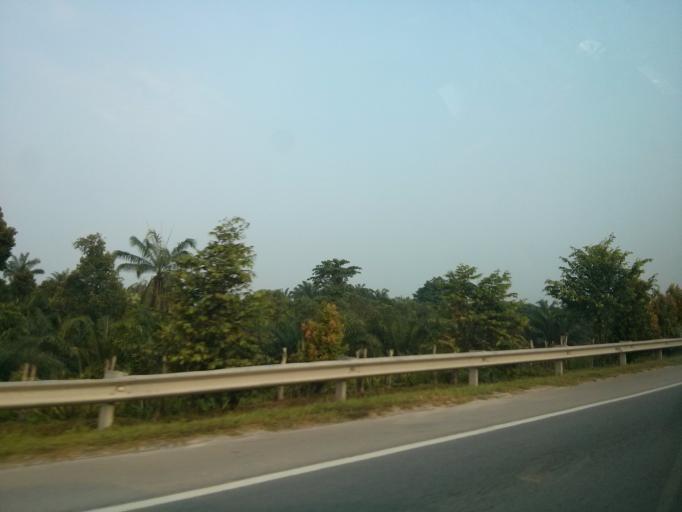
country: MY
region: Putrajaya
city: Putrajaya
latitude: 2.8666
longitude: 101.6873
